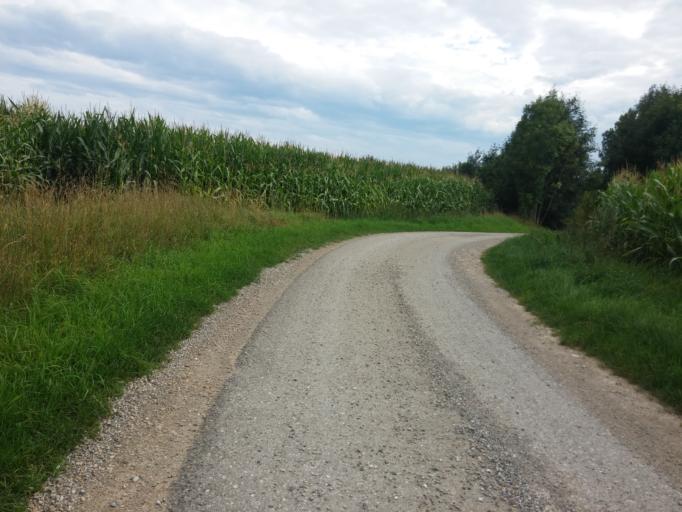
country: DE
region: Baden-Wuerttemberg
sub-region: Tuebingen Region
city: Aitrach
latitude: 47.9323
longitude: 10.0929
